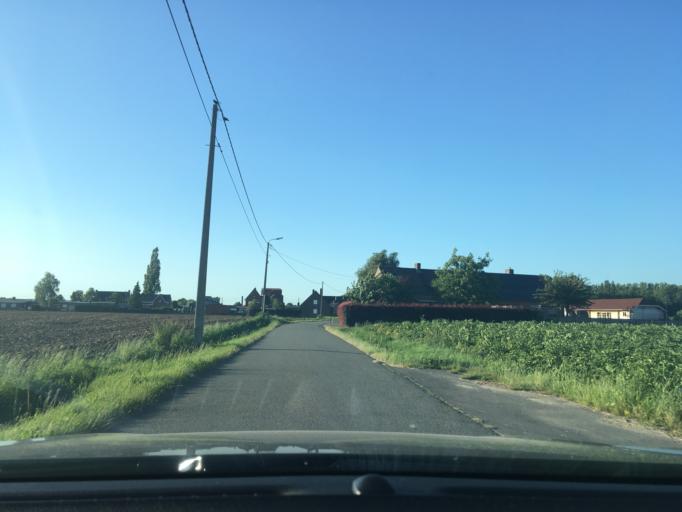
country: BE
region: Flanders
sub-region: Provincie West-Vlaanderen
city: Hooglede
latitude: 51.0134
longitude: 3.0943
